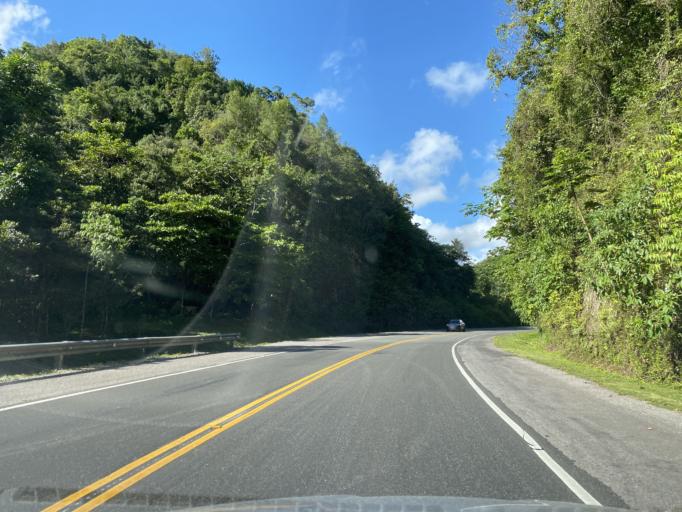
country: DO
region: Monte Plata
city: Majagual
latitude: 19.0626
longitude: -69.8287
